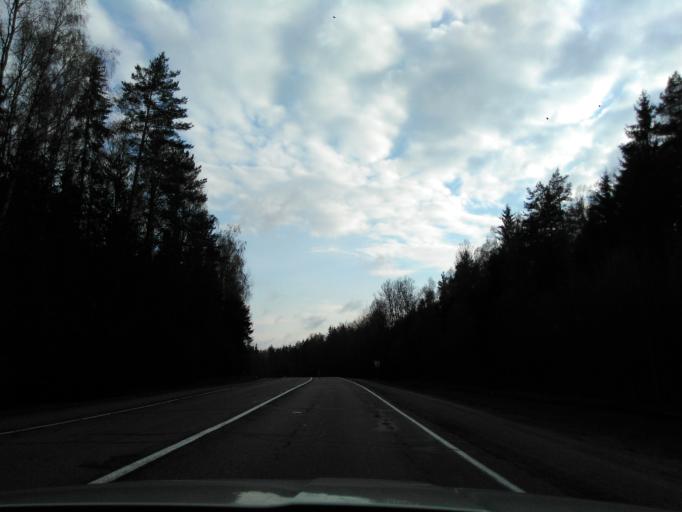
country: BY
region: Minsk
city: Lahoysk
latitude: 54.2826
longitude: 27.8650
